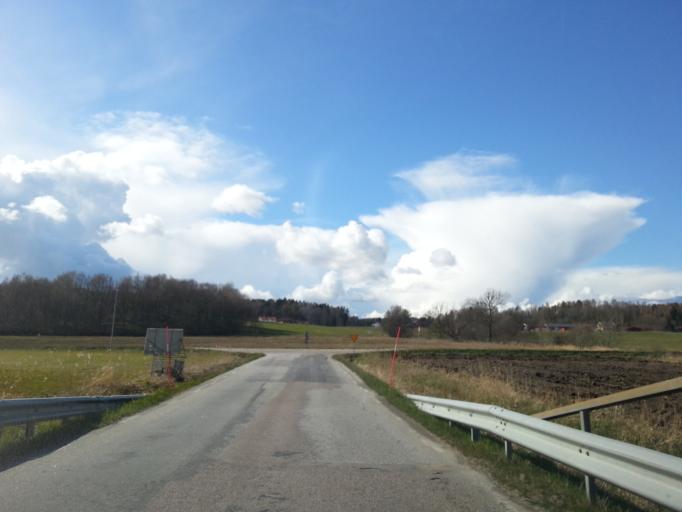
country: SE
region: Vaestra Goetaland
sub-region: Ale Kommun
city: Nodinge-Nol
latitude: 57.9283
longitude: 12.0396
